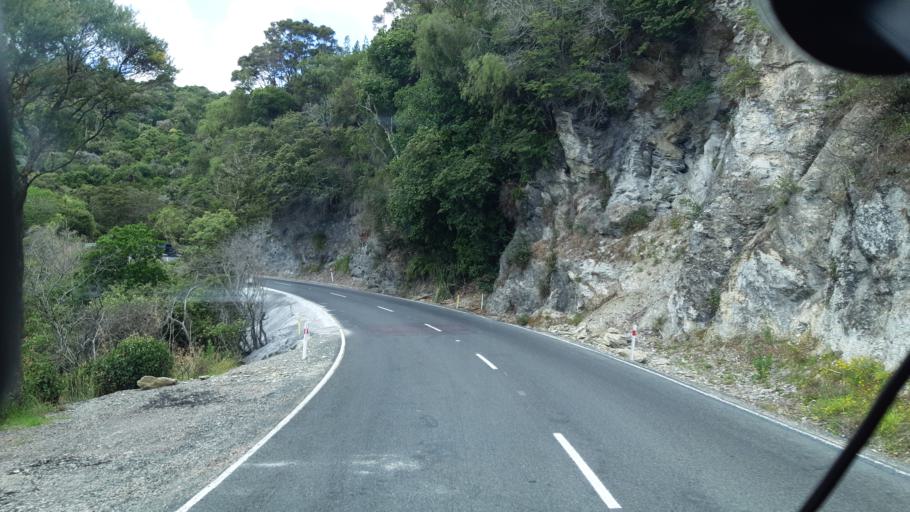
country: NZ
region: Northland
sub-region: Far North District
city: Taipa
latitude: -35.2453
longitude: 173.5352
